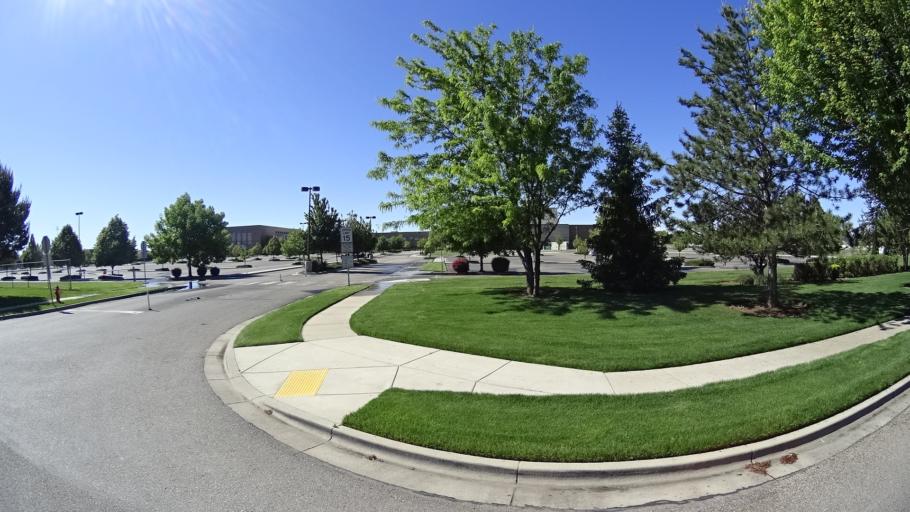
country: US
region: Idaho
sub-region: Ada County
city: Meridian
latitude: 43.6558
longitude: -116.4118
